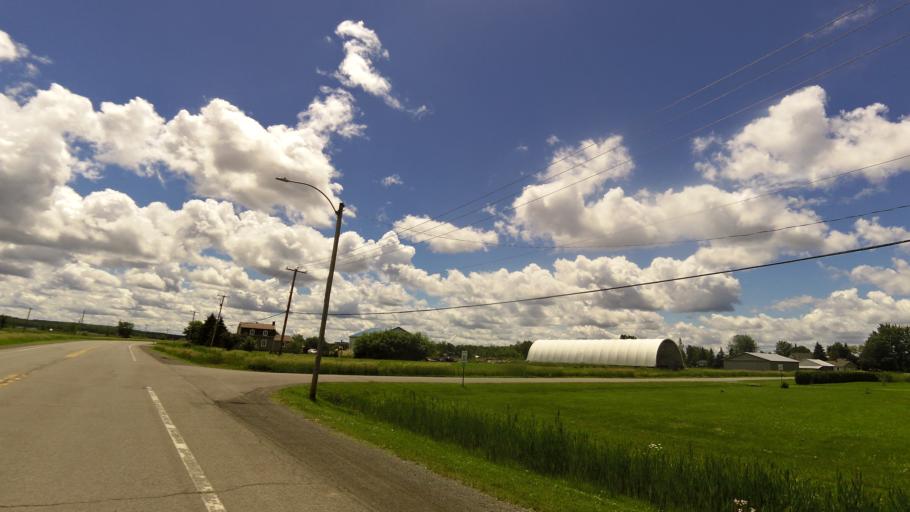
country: CA
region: Quebec
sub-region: Monteregie
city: Hudson
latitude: 45.5237
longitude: -74.1706
